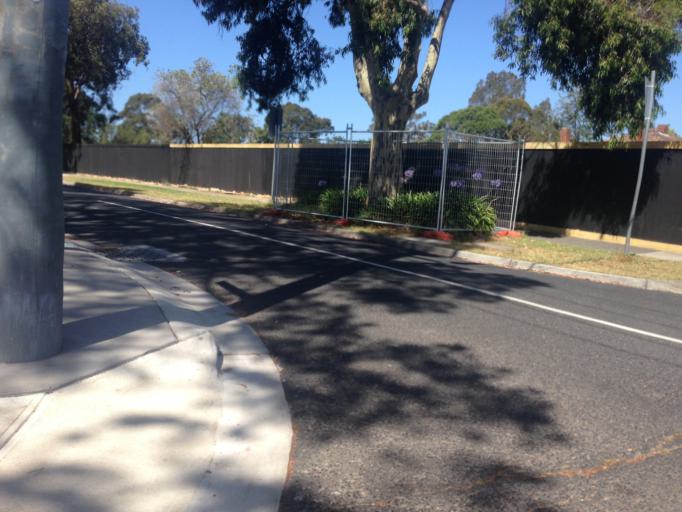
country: AU
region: Victoria
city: Ivanhoe East
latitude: -37.7744
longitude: 145.0522
